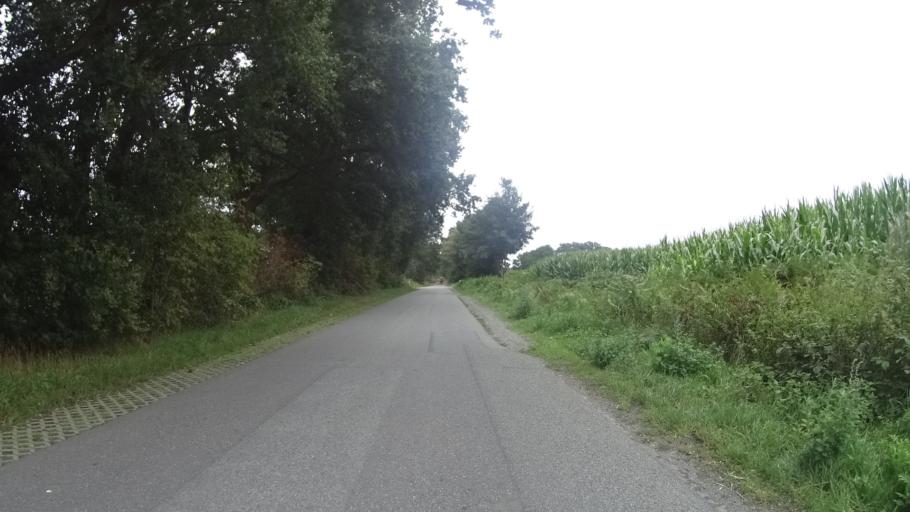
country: DE
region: Lower Saxony
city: Stinstedt
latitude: 53.6566
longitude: 8.9661
